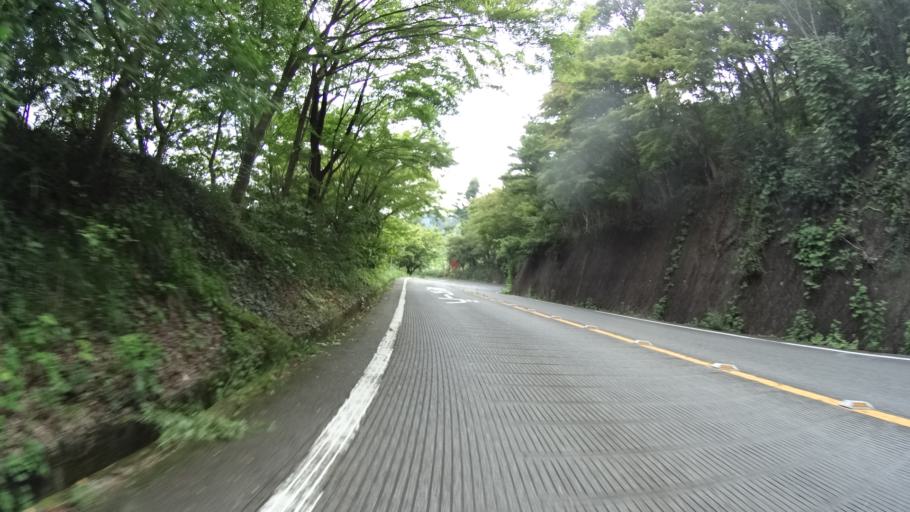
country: JP
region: Yamanashi
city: Kofu-shi
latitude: 35.6981
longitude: 138.5609
